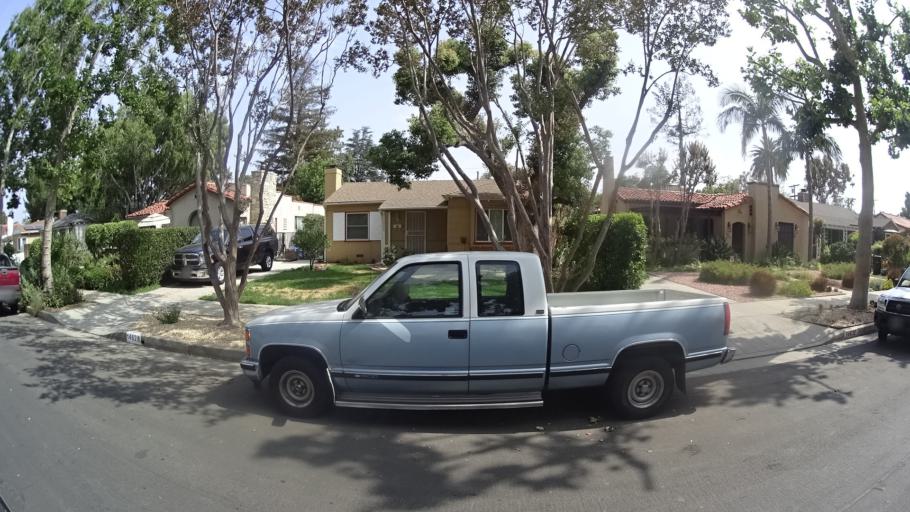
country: US
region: California
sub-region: Los Angeles County
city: Van Nuys
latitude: 34.1712
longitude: -118.4519
